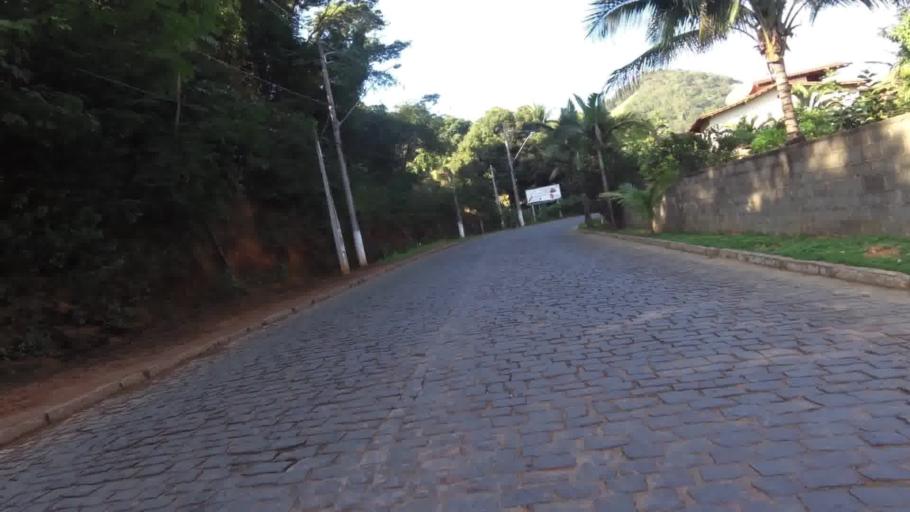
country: BR
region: Espirito Santo
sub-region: Alfredo Chaves
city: Alfredo Chaves
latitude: -20.6318
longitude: -40.7592
